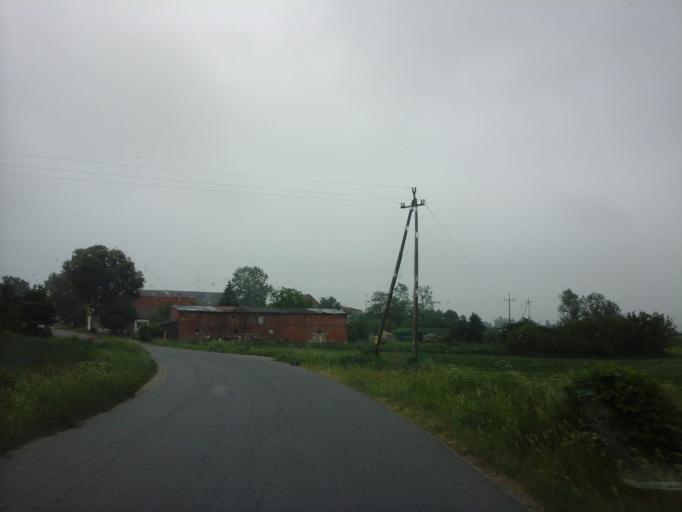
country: PL
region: West Pomeranian Voivodeship
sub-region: Powiat choszczenski
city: Pelczyce
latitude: 53.0874
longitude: 15.3499
